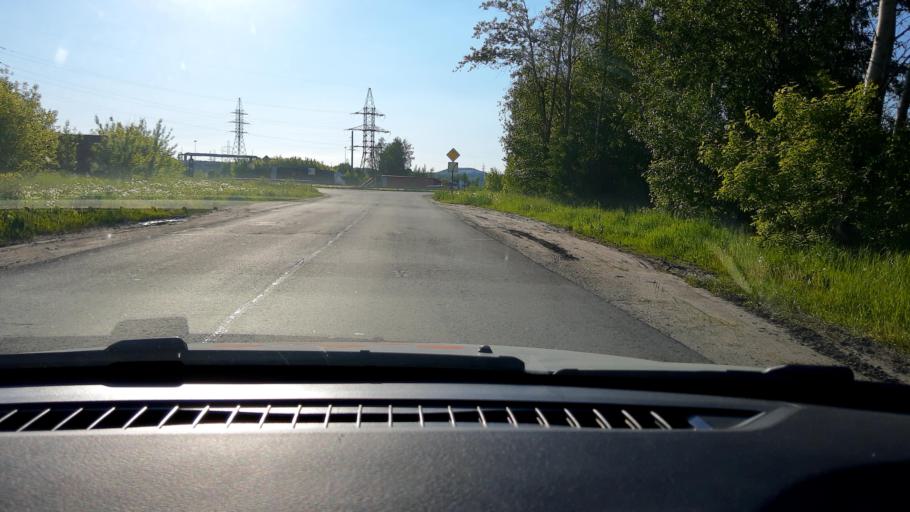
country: RU
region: Nizjnij Novgorod
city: Kstovo
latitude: 56.1044
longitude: 44.1295
